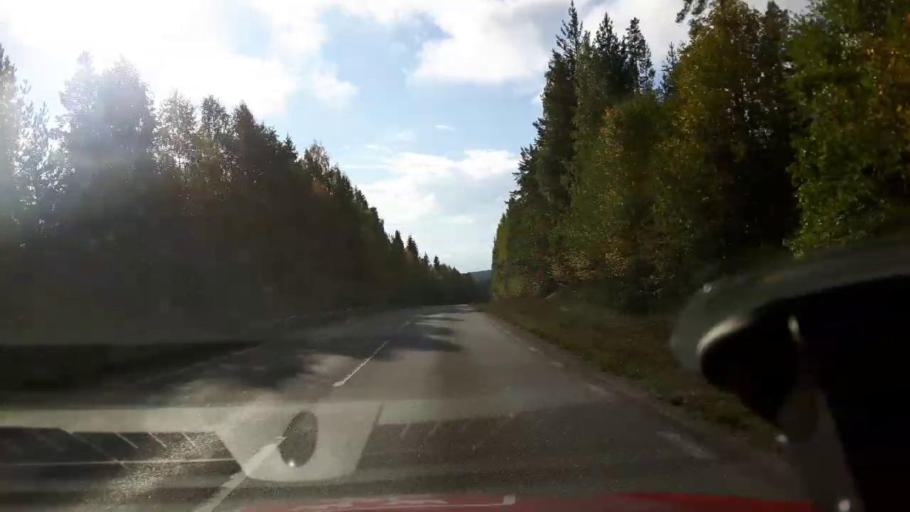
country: SE
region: Vaesternorrland
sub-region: Ange Kommun
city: Ange
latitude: 62.0797
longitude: 15.0990
